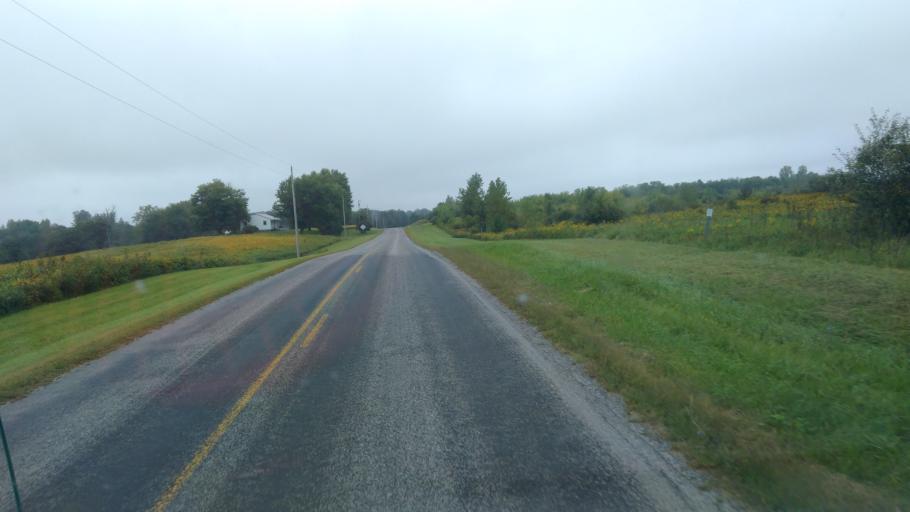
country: US
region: Ohio
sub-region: Hardin County
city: Kenton
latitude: 40.5698
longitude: -83.6346
